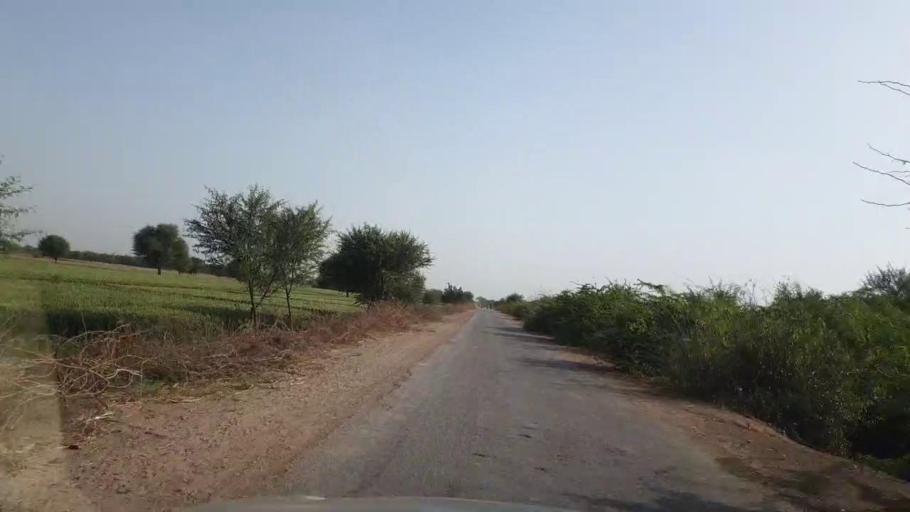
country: PK
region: Sindh
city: Tando Ghulam Ali
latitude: 25.0950
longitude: 68.8689
